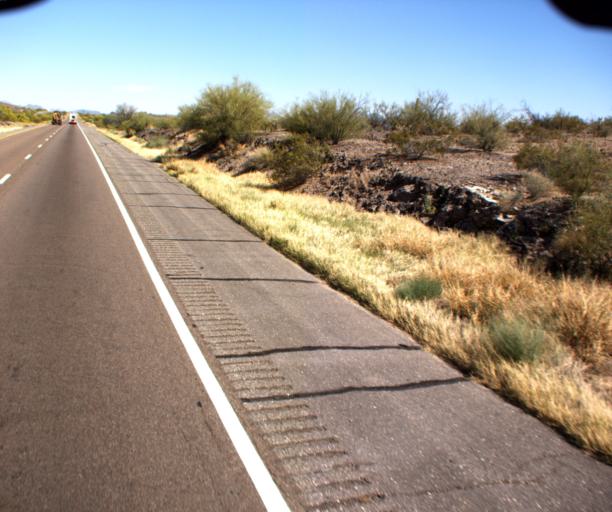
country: US
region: Arizona
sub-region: Pinal County
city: Maricopa
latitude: 32.8495
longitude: -112.3361
